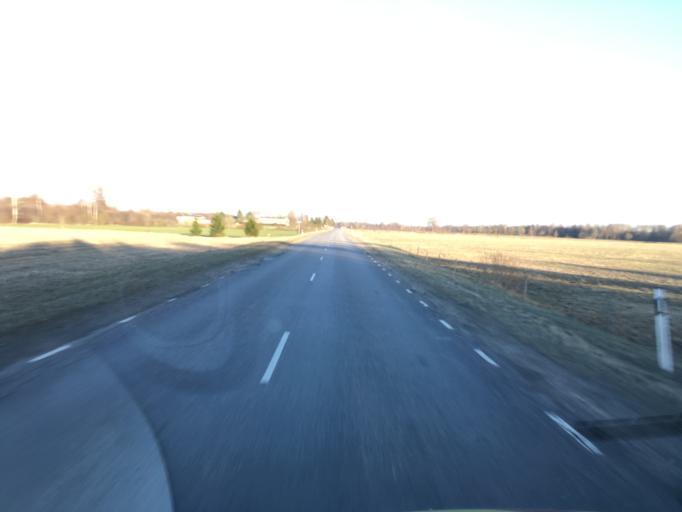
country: EE
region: Raplamaa
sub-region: Rapla vald
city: Rapla
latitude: 59.0852
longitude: 24.8164
